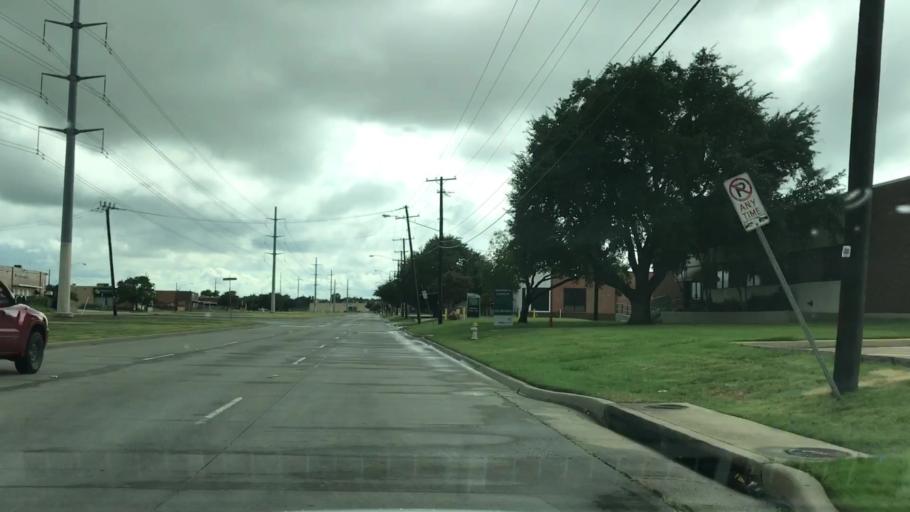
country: US
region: Texas
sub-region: Dallas County
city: Irving
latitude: 32.8203
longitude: -96.8952
